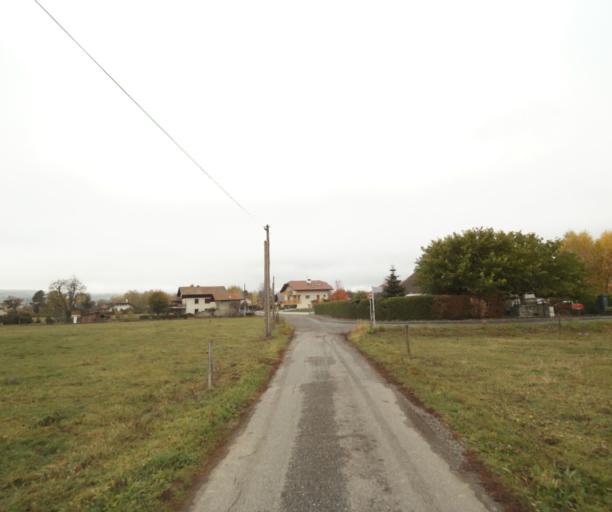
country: FR
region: Rhone-Alpes
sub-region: Departement de la Haute-Savoie
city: Reignier-Esery
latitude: 46.1330
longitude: 6.2849
